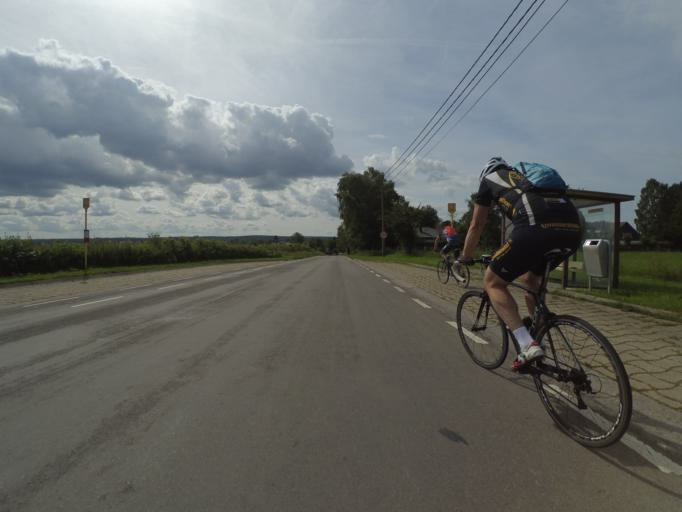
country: BE
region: Wallonia
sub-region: Province de Liege
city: Eupen
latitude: 50.6548
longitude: 6.0390
